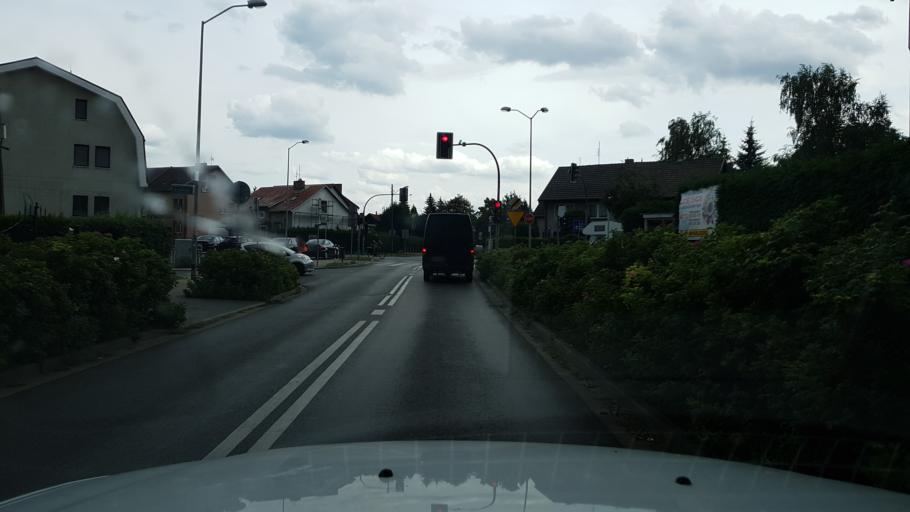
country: PL
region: West Pomeranian Voivodeship
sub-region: Powiat policki
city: Przeclaw
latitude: 53.4204
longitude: 14.4862
